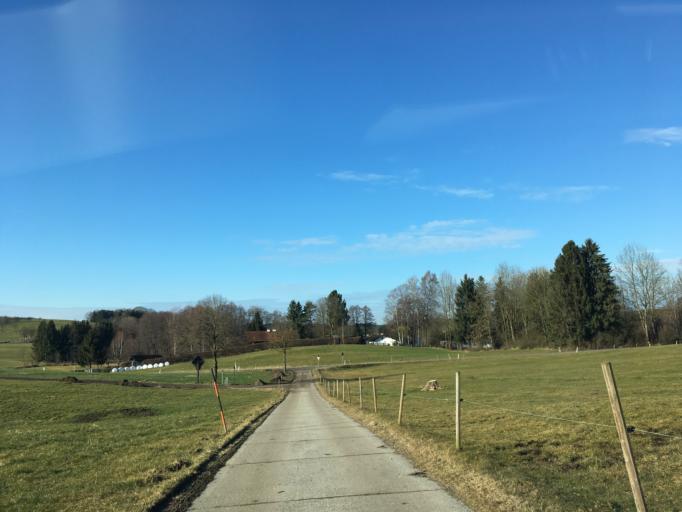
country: DE
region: Bavaria
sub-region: Upper Bavaria
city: Riedering
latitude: 47.8238
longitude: 12.2133
